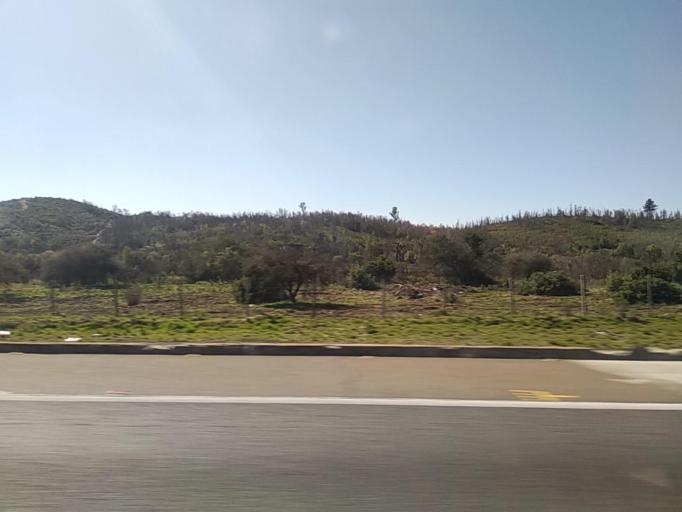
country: CL
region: Valparaiso
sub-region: Provincia de Marga Marga
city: Quilpue
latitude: -33.1963
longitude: -71.4932
